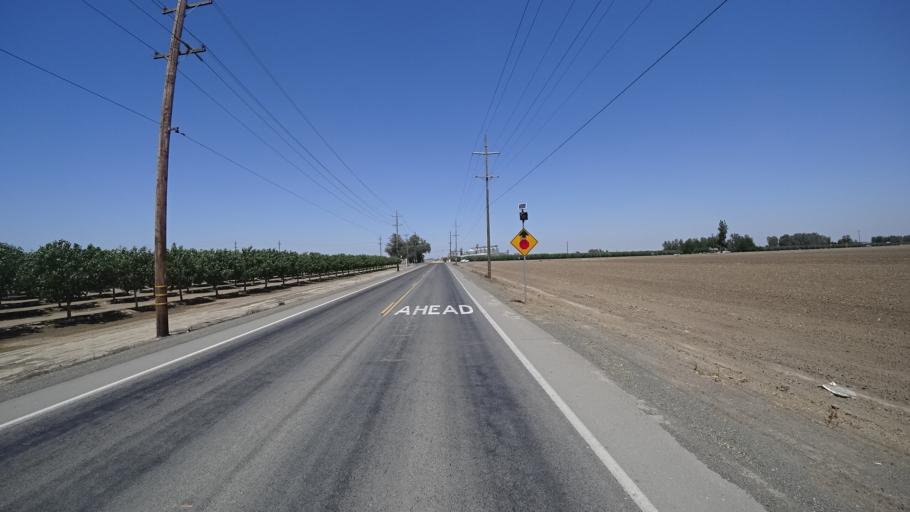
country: US
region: California
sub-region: Kings County
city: Home Garden
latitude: 36.2095
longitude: -119.6459
